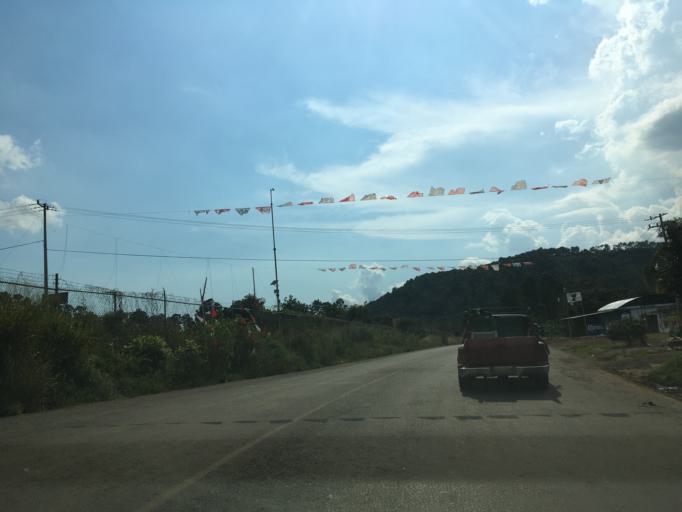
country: MX
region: Michoacan
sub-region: Ziracuaretiro
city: Patuan
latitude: 19.4415
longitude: -101.8842
